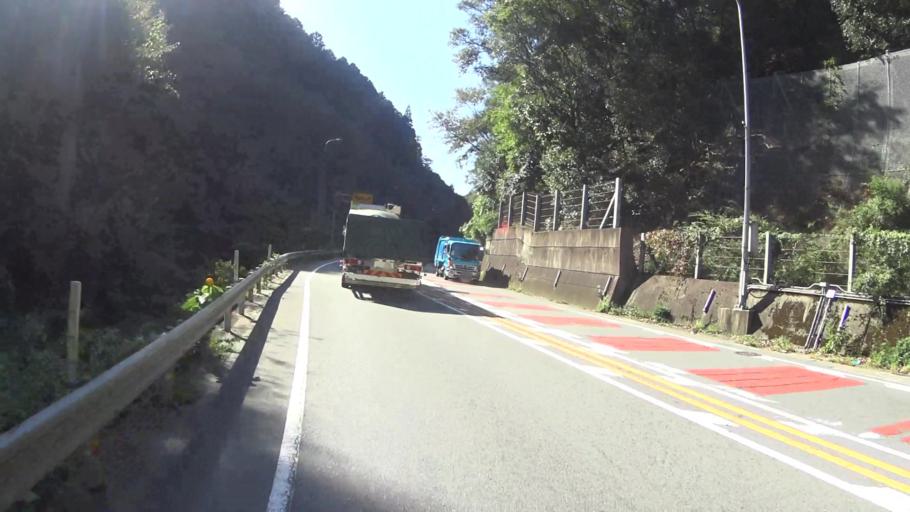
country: JP
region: Kyoto
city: Muko
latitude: 34.9829
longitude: 135.6440
